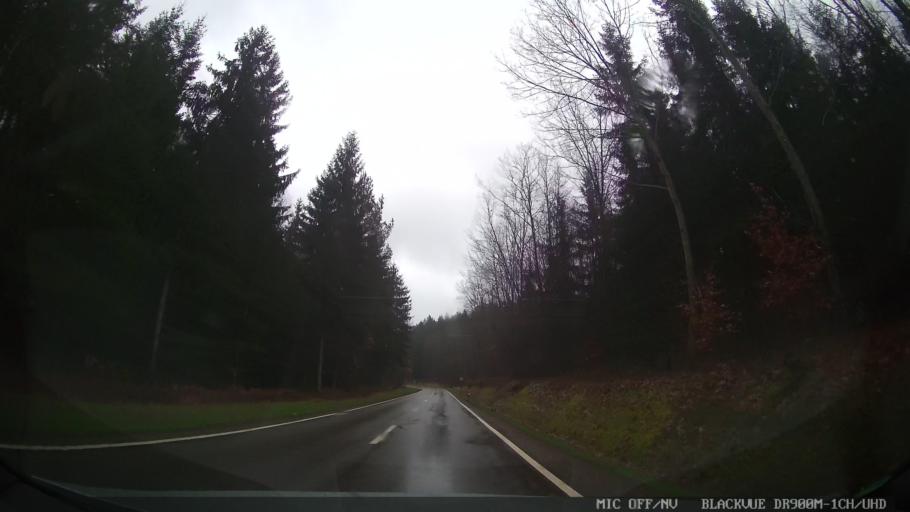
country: DE
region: Saarland
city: Britten
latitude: 49.4912
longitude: 6.6692
